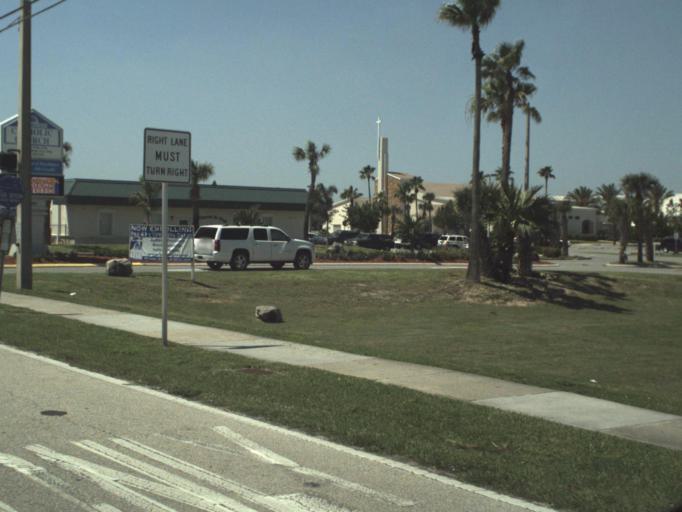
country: US
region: Florida
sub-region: Brevard County
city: Indian Harbour Beach
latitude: 28.1356
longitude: -80.5803
